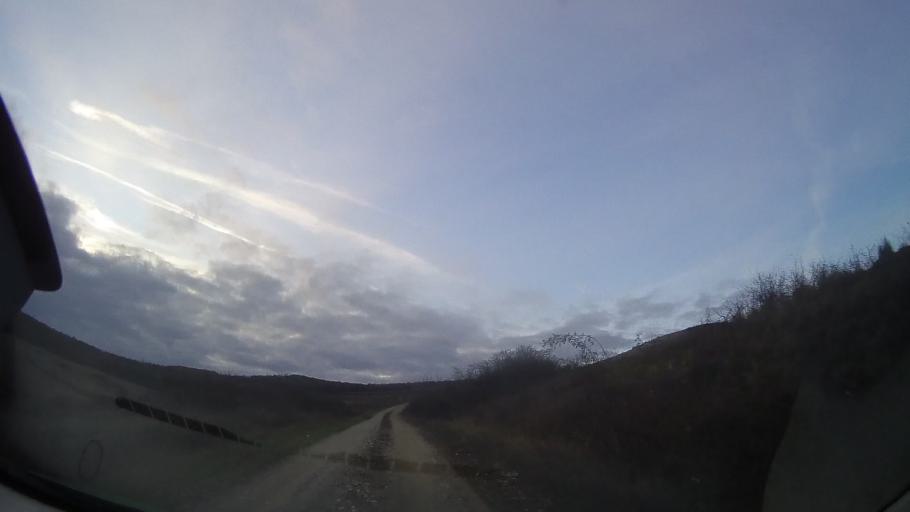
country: RO
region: Cluj
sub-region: Comuna Palatca
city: Palatca
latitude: 46.8572
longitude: 24.0351
